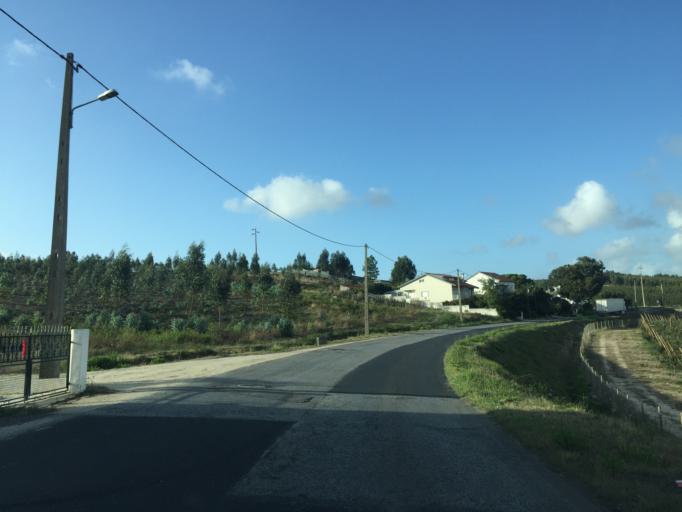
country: PT
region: Lisbon
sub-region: Torres Vedras
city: Torres Vedras
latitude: 39.1185
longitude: -9.2638
